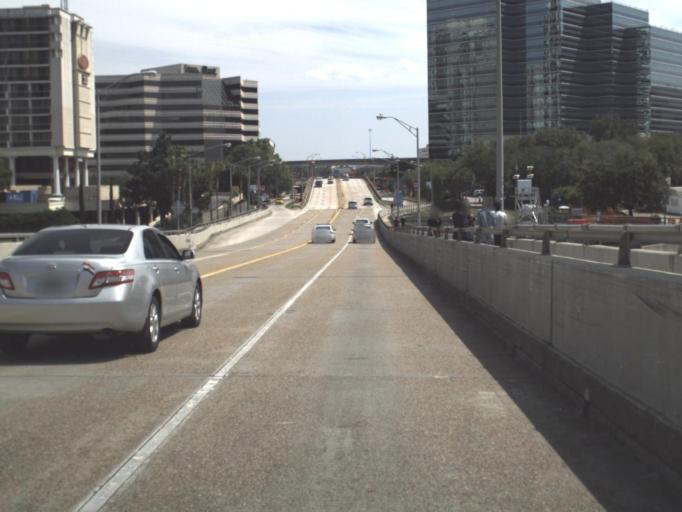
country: US
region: Florida
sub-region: Duval County
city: Jacksonville
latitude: 30.3215
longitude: -81.6587
